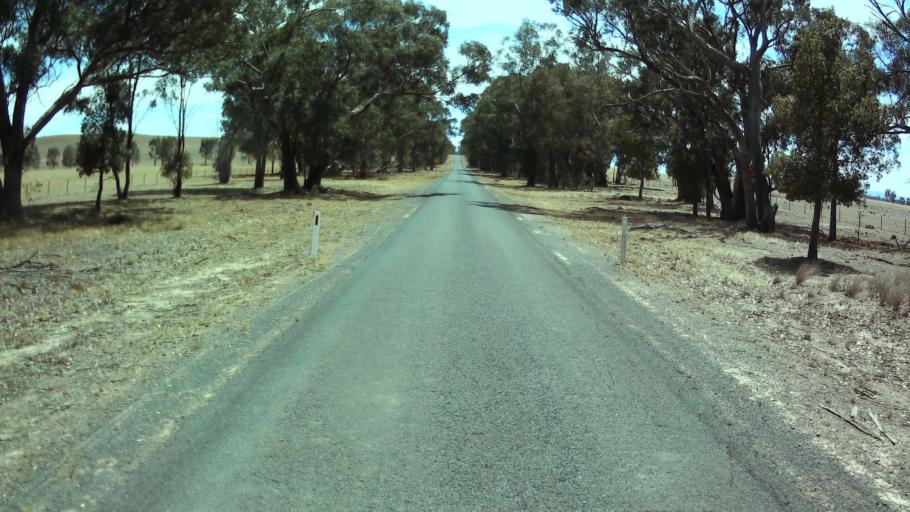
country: AU
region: New South Wales
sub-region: Weddin
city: Grenfell
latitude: -33.7649
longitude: 148.2044
